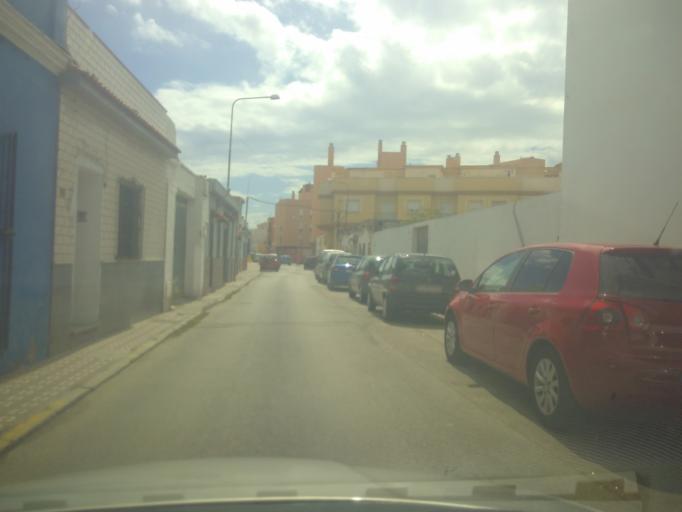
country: ES
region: Andalusia
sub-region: Provincia de Cadiz
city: La Linea de la Concepcion
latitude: 36.1687
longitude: -5.3434
